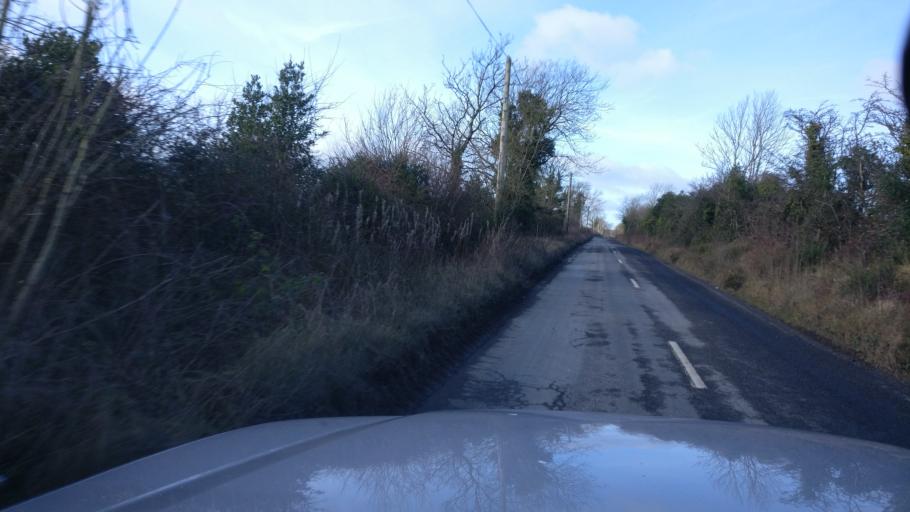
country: IE
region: Leinster
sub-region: Kilkenny
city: Castlecomer
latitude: 52.8949
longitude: -7.1702
